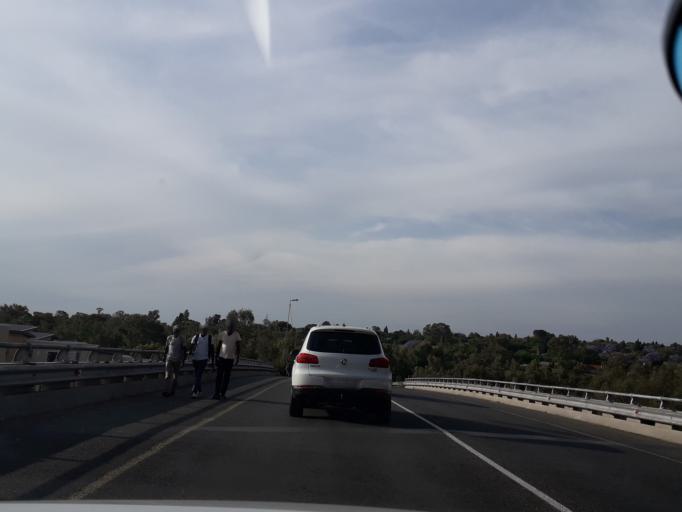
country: ZA
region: Gauteng
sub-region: City of Johannesburg Metropolitan Municipality
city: Diepsloot
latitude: -26.0485
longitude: 27.9993
